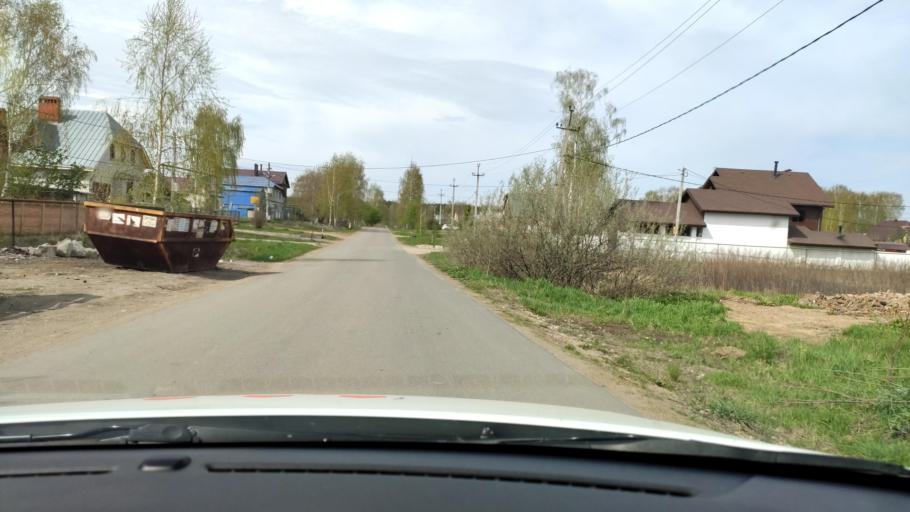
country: RU
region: Tatarstan
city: Osinovo
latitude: 55.8072
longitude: 48.8868
